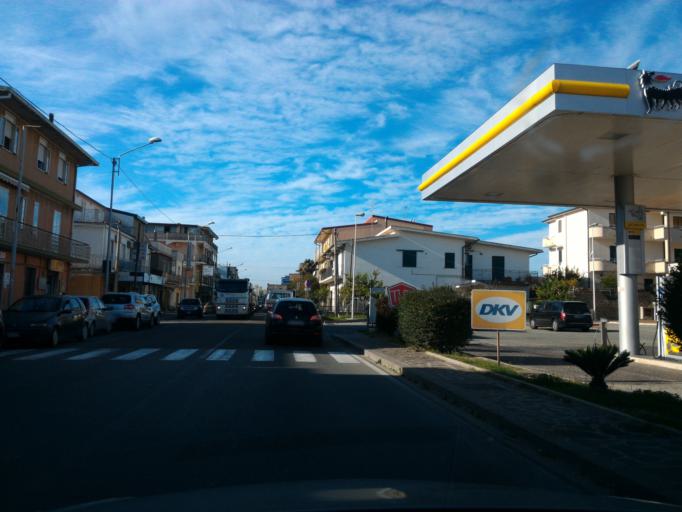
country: IT
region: Calabria
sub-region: Provincia di Catanzaro
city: Botricello
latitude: 38.9343
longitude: 16.8536
